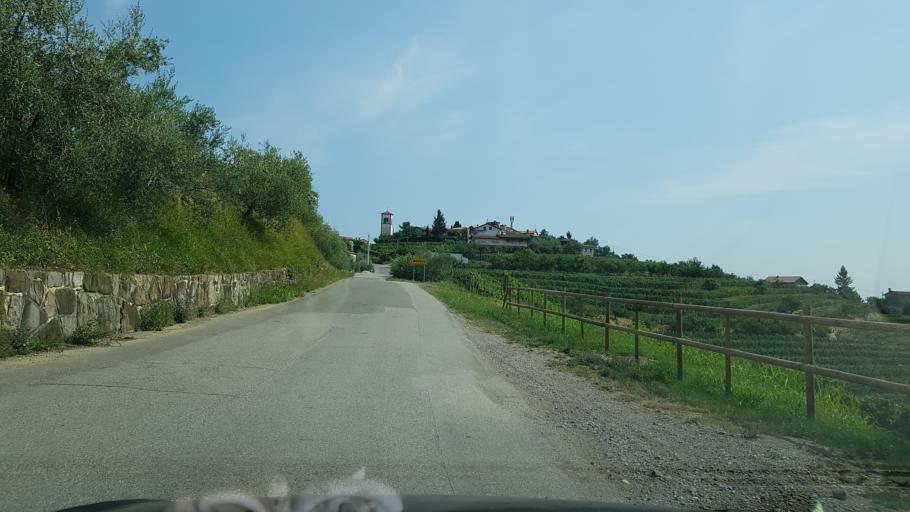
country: SI
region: Brda
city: Dobrovo
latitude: 45.9885
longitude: 13.5203
